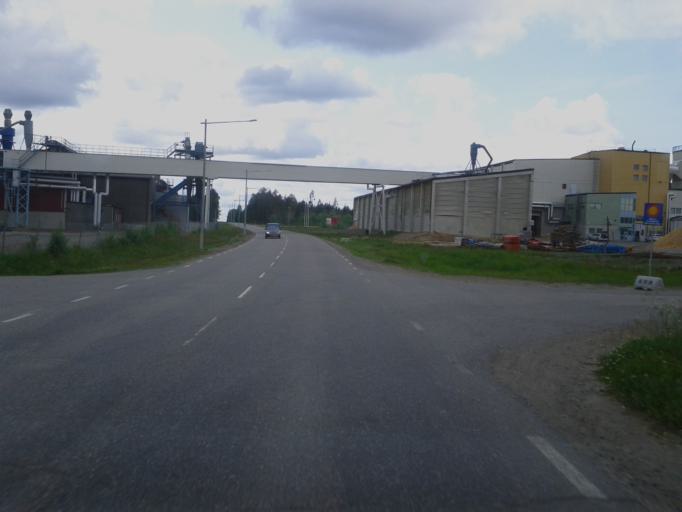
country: SE
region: Vaesterbotten
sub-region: Mala Kommun
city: Mala
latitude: 65.1929
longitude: 18.7225
